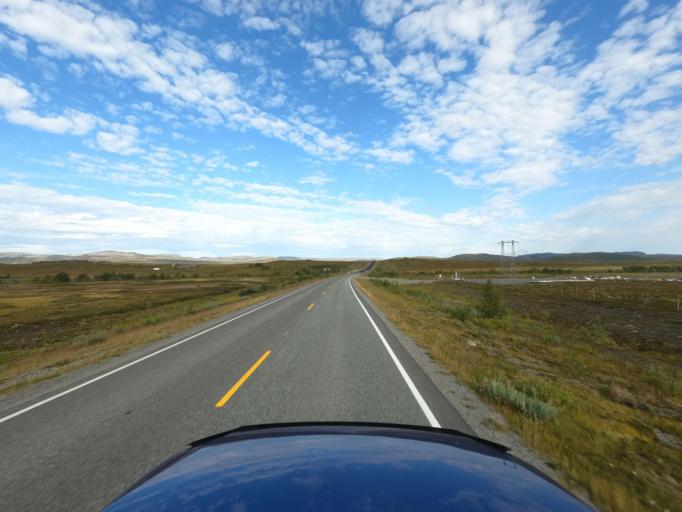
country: NO
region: Finnmark Fylke
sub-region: Kvalsund
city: Kvalsund
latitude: 70.2307
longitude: 24.0791
